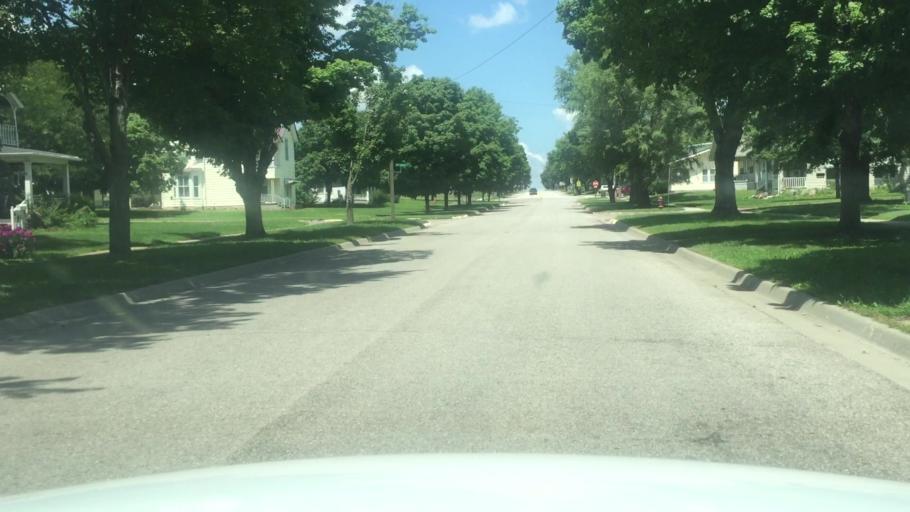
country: US
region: Kansas
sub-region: Brown County
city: Horton
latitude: 39.6659
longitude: -95.5273
